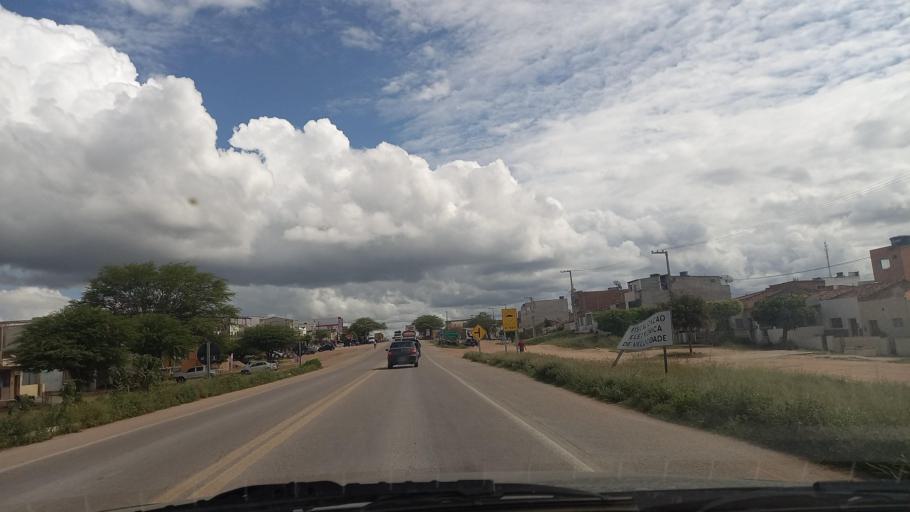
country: BR
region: Pernambuco
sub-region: Cachoeirinha
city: Cachoeirinha
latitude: -8.4887
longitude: -36.2315
